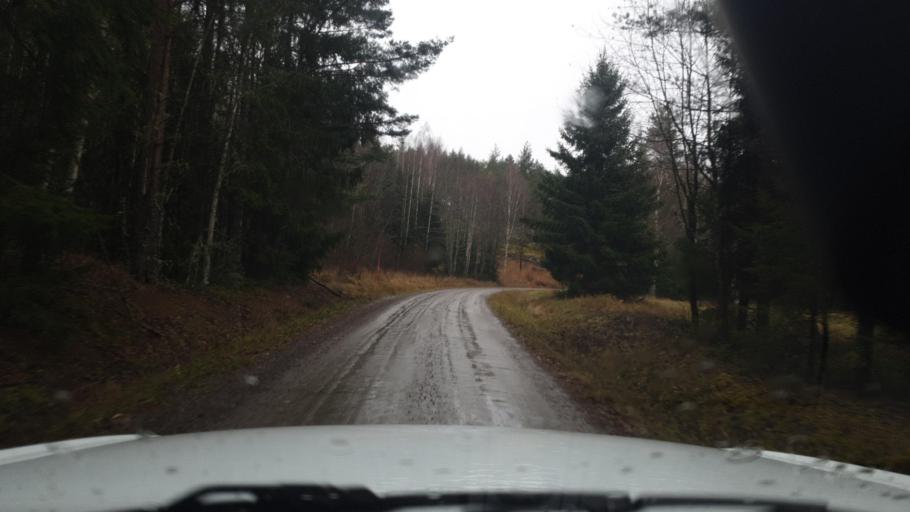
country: SE
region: Vaermland
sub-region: Grums Kommun
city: Grums
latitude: 59.5143
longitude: 12.9282
